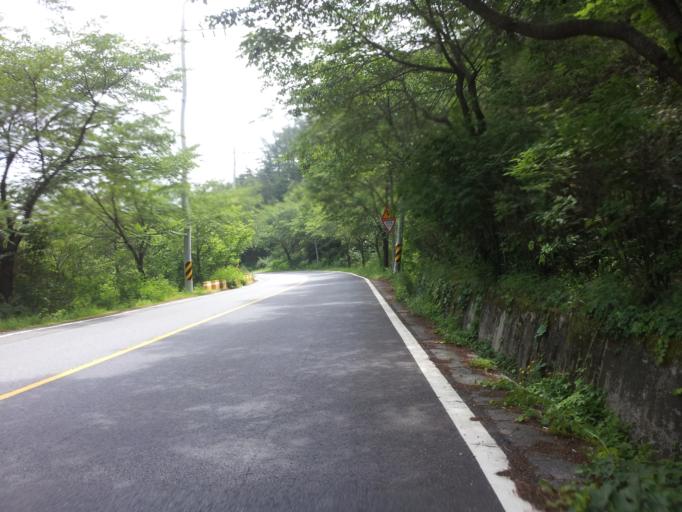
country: KR
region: Chungcheongbuk-do
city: Okcheon
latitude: 36.3909
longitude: 127.5241
